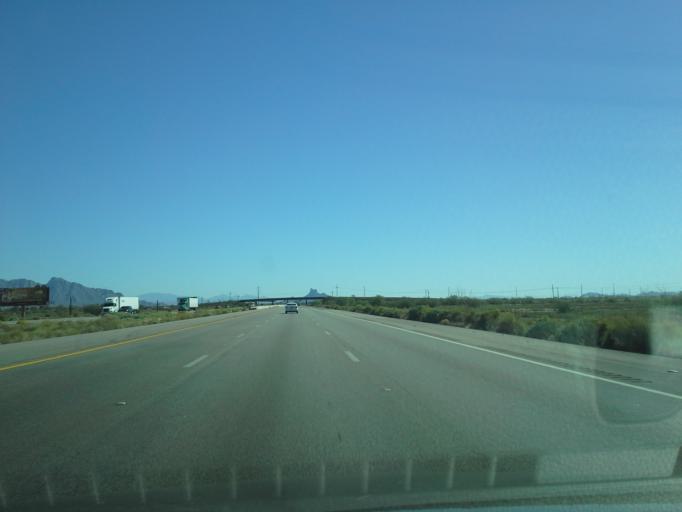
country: US
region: Arizona
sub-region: Pinal County
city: Eloy
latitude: 32.7519
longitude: -111.5790
